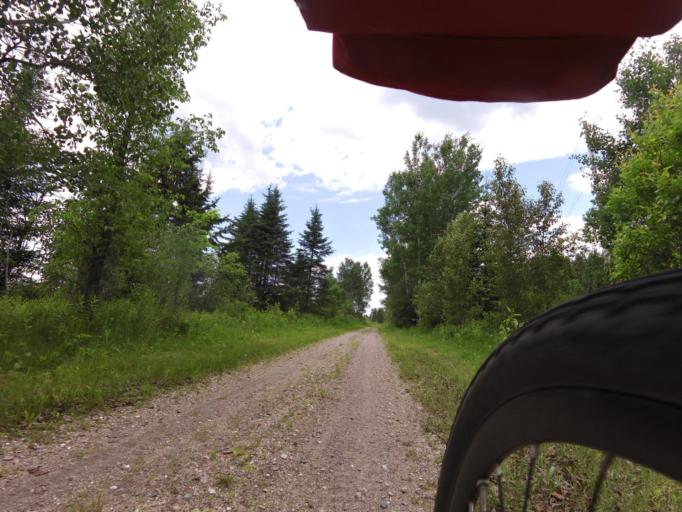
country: CA
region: Quebec
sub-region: Outaouais
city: Maniwaki
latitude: 46.0408
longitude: -76.0985
